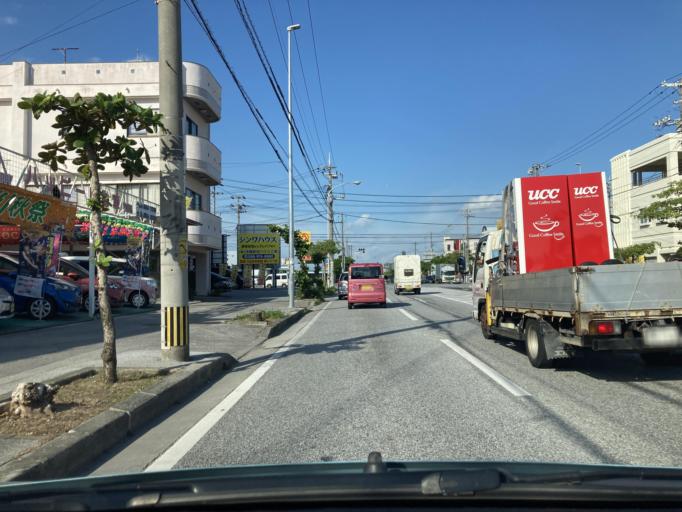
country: JP
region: Okinawa
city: Okinawa
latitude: 26.3205
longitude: 127.8321
